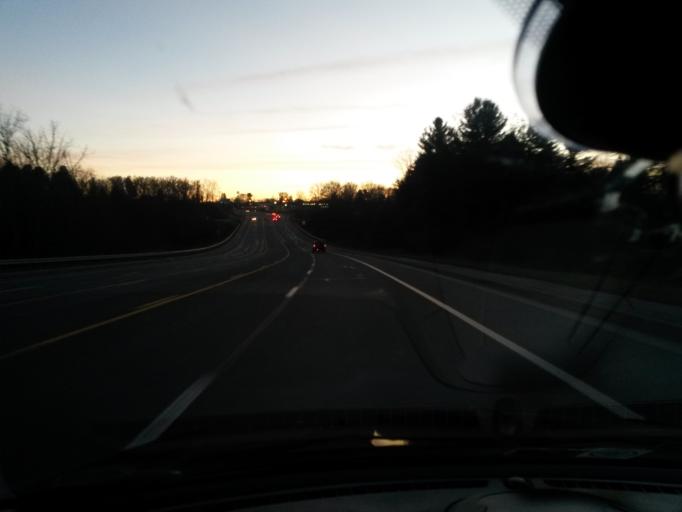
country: US
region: West Virginia
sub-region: Raleigh County
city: Beckley
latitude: 37.7776
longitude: -81.1576
